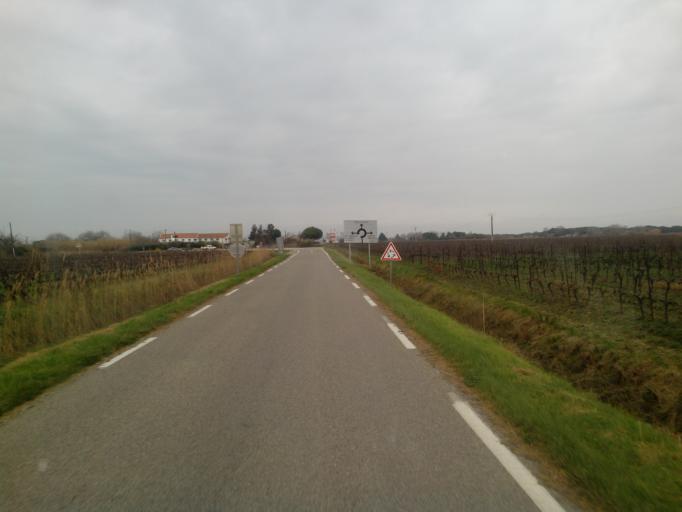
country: FR
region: Languedoc-Roussillon
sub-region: Departement du Gard
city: Aigues-Mortes
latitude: 43.5719
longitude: 4.3107
